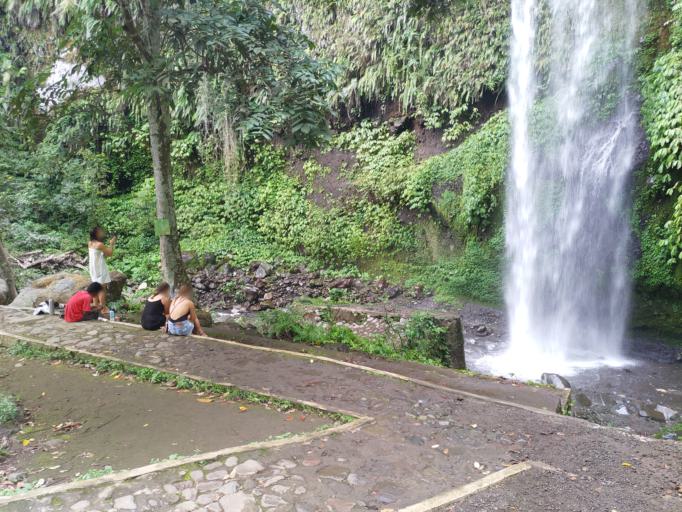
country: ID
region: West Nusa Tenggara
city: Bayan
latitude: -8.3064
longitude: 116.4081
